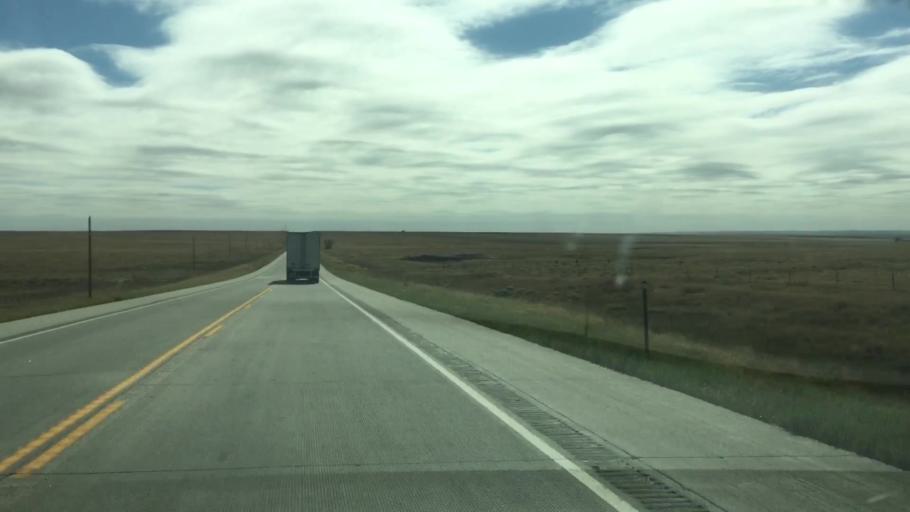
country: US
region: Colorado
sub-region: Lincoln County
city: Hugo
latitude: 39.0002
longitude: -103.2856
